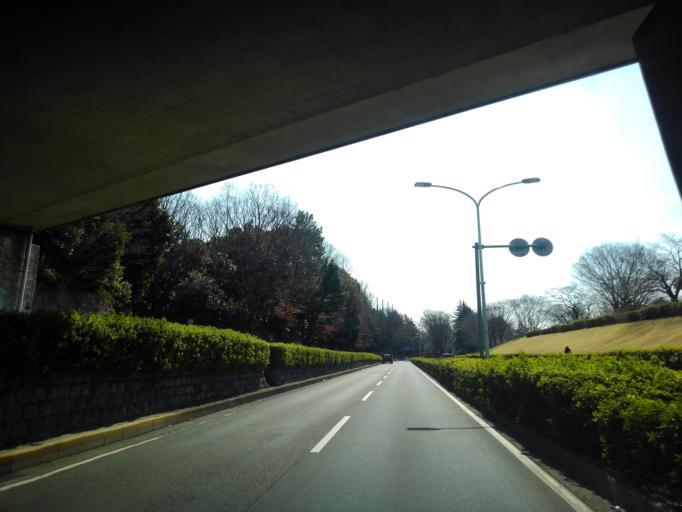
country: JP
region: Saitama
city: Tokorozawa
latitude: 35.7975
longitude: 139.4691
